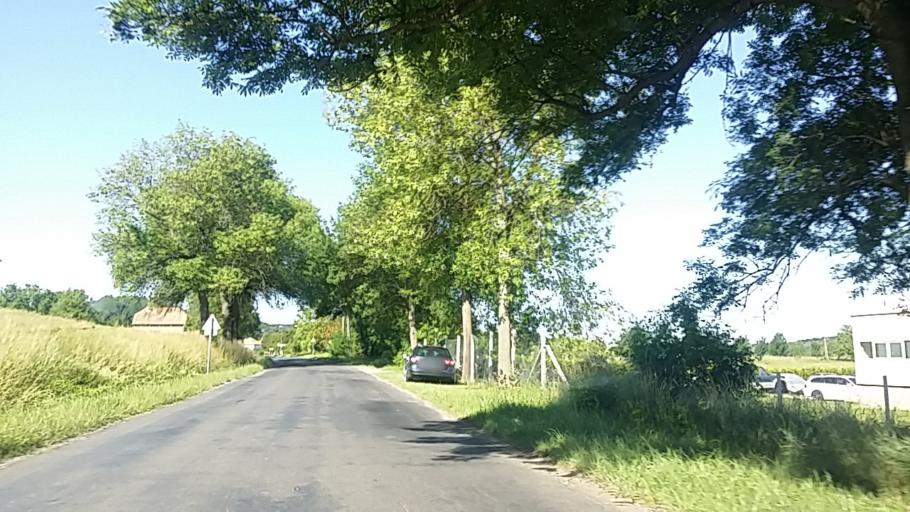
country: HU
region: Zala
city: Zalalovo
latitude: 46.8668
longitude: 16.7156
